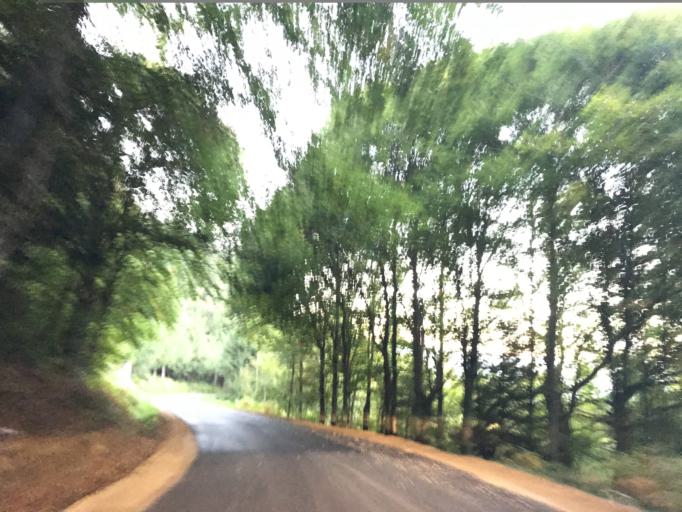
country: FR
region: Auvergne
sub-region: Departement du Puy-de-Dome
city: Celles-sur-Durolle
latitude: 45.8135
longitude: 3.6599
